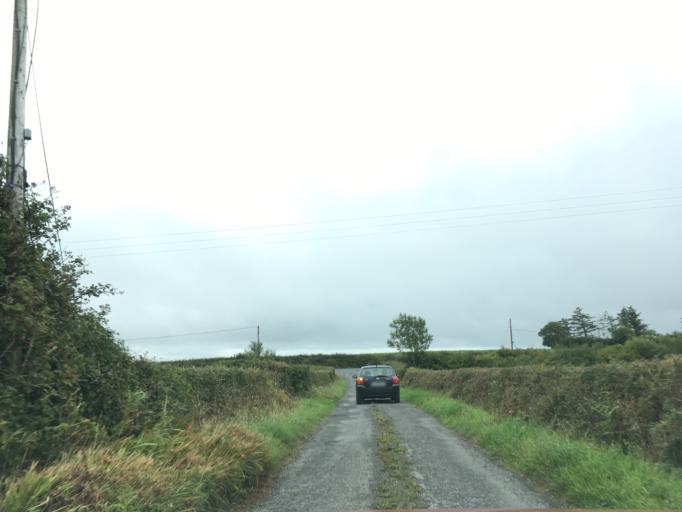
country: IE
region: Munster
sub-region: An Clar
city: Ennis
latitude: 52.7191
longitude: -9.0941
